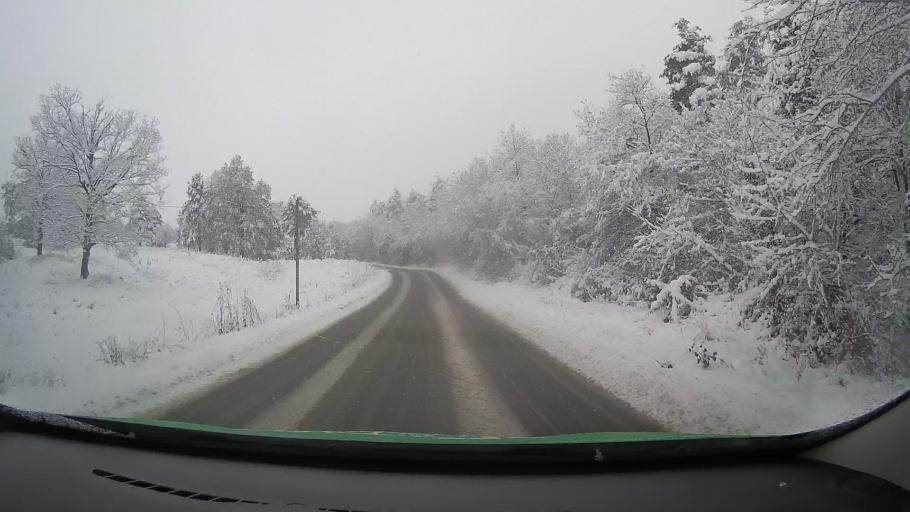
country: RO
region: Hunedoara
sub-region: Comuna Teliucu Inferior
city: Teliucu Inferior
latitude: 45.7067
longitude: 22.8820
